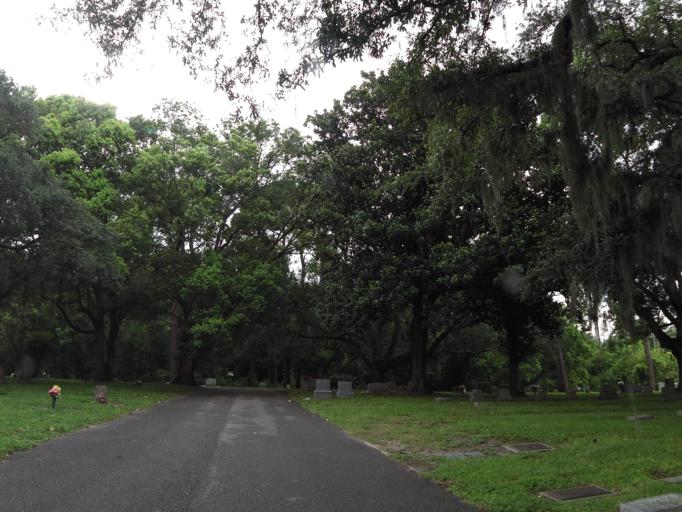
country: US
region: Florida
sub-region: Duval County
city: Jacksonville
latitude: 30.2985
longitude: -81.6214
